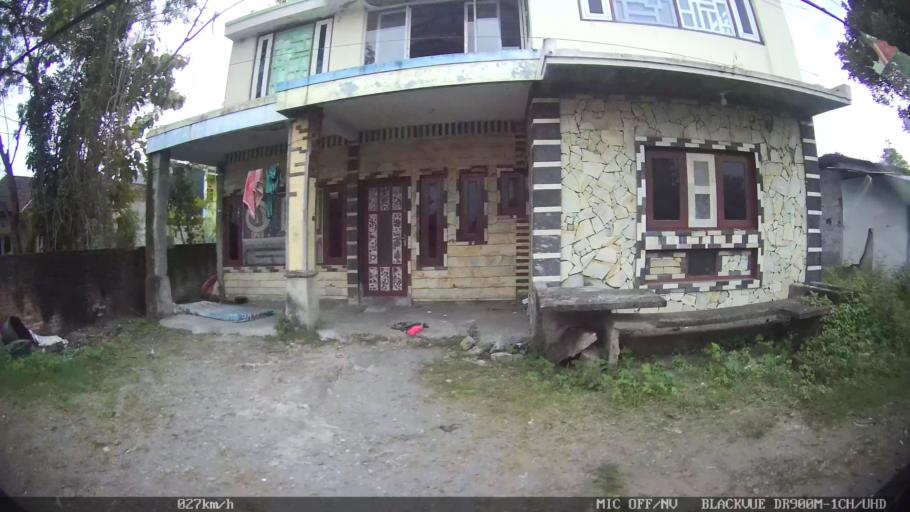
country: ID
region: Daerah Istimewa Yogyakarta
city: Depok
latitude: -7.8114
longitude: 110.4175
